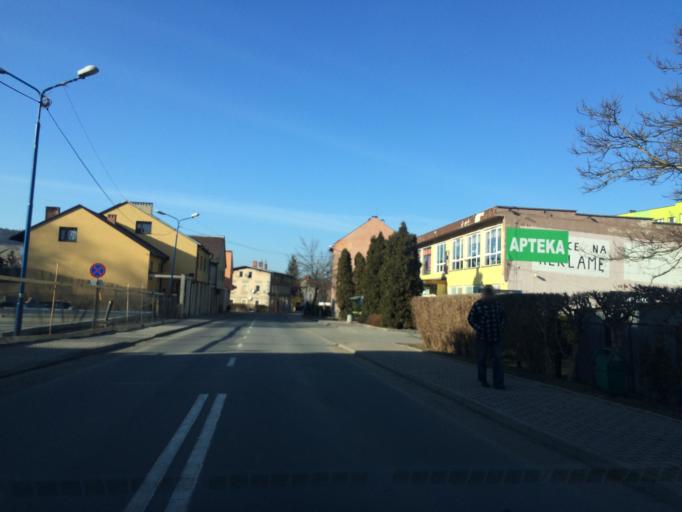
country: PL
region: Lower Silesian Voivodeship
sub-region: Powiat klodzki
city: Stronie Slaskie
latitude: 50.2957
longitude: 16.8747
